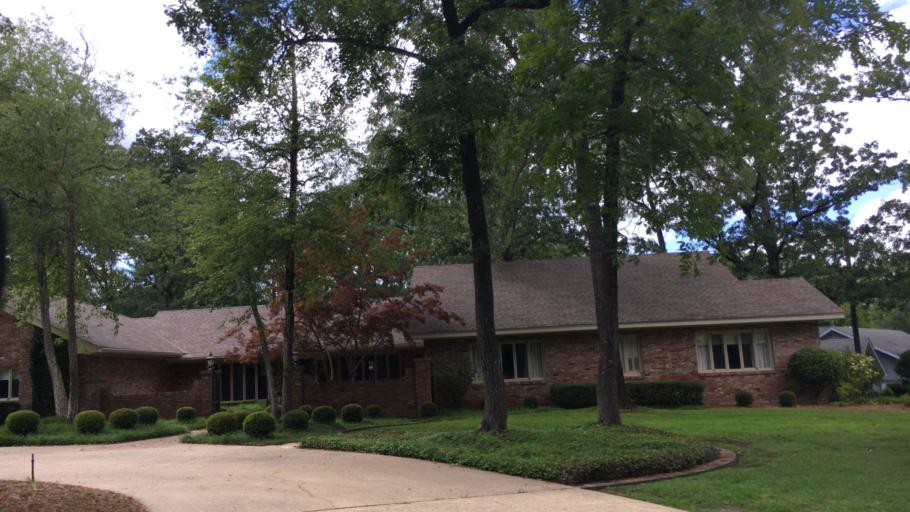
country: US
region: Louisiana
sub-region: Lincoln Parish
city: Ruston
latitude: 32.5482
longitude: -92.6345
